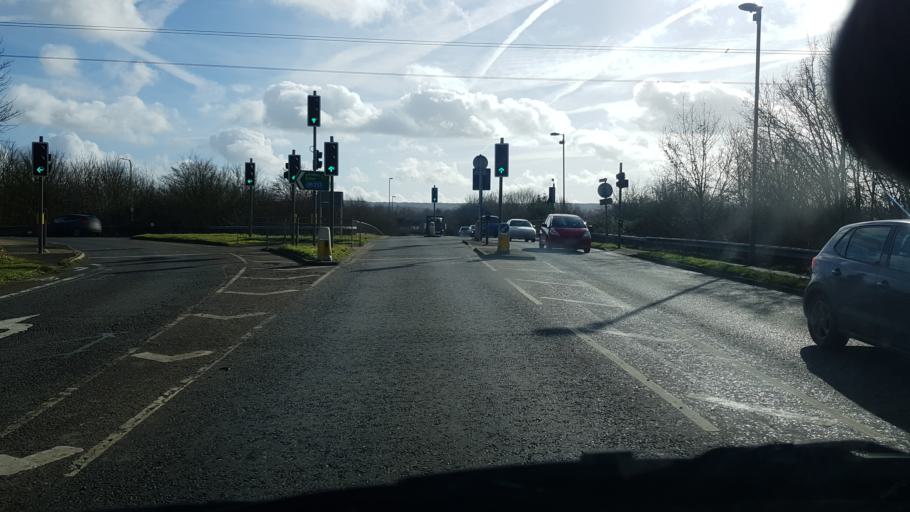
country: GB
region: England
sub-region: Surrey
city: Send
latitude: 51.2648
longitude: -0.5511
